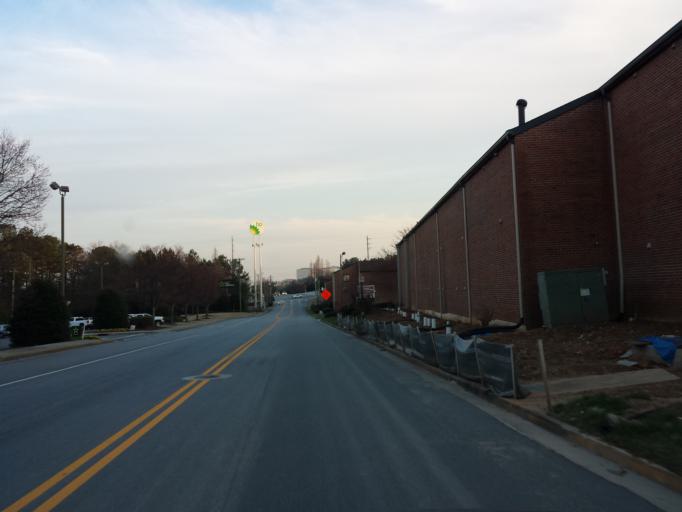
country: US
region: Georgia
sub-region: Cobb County
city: Vinings
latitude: 33.9050
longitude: -84.4737
